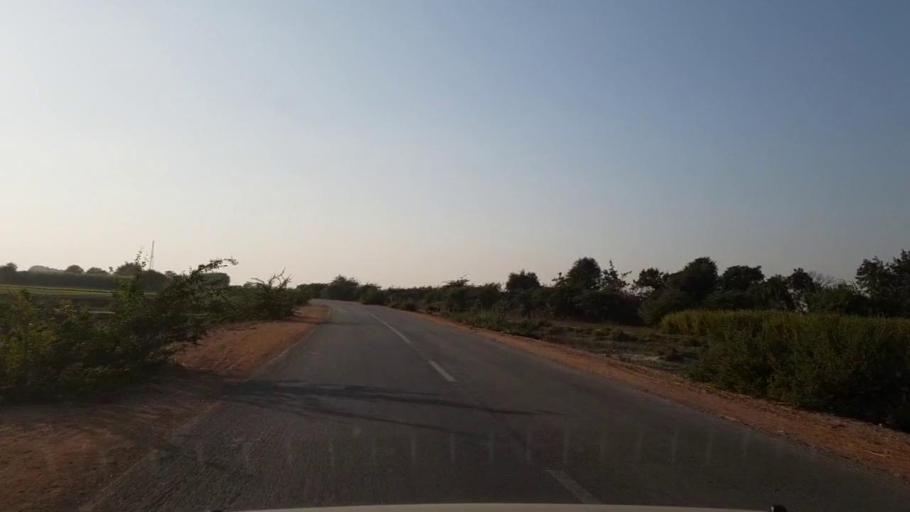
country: PK
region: Sindh
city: Mirpur Batoro
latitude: 24.6873
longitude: 68.1740
